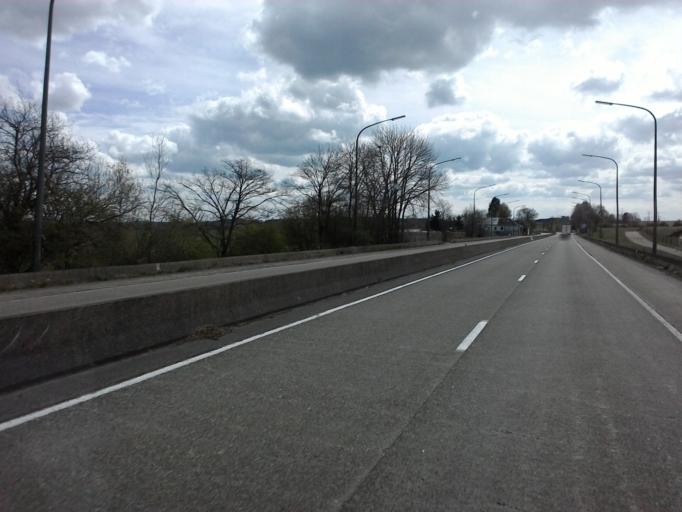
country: BE
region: Wallonia
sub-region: Province du Luxembourg
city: Martelange
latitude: 49.8706
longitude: 5.7108
